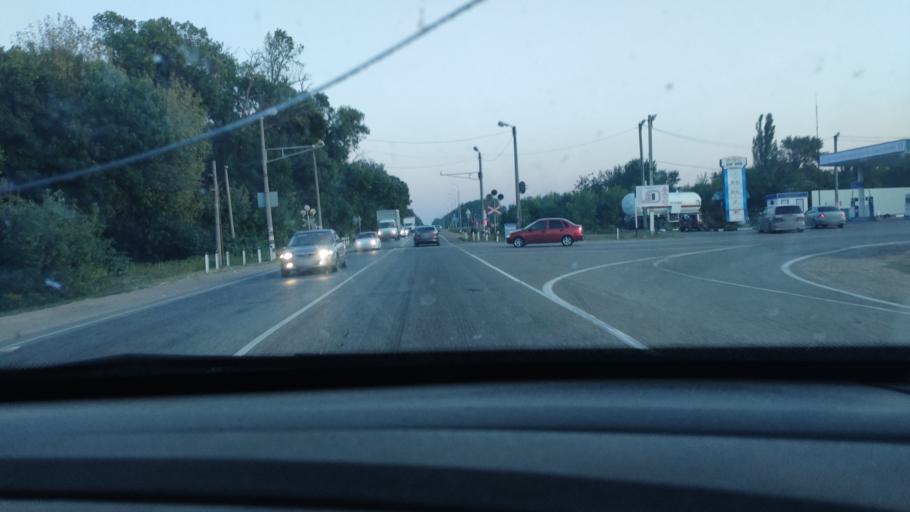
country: RU
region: Krasnodarskiy
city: Medvedovskaya
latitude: 45.4489
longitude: 38.9923
